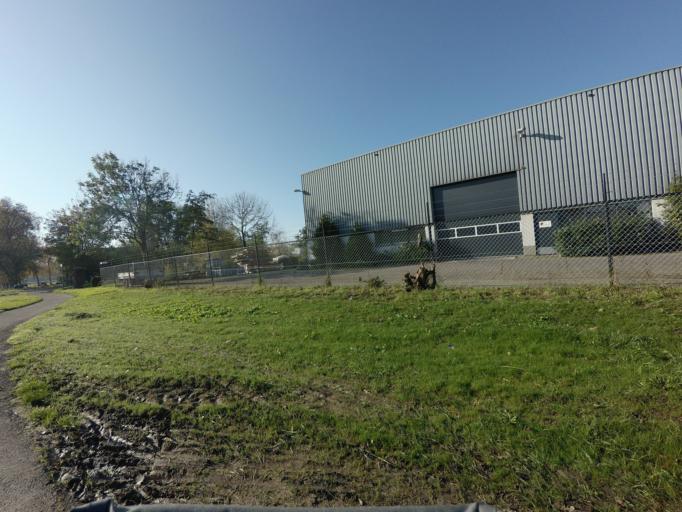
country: NL
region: North Brabant
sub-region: Gemeente Werkendam
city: Werkendam
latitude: 51.7995
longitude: 4.8870
